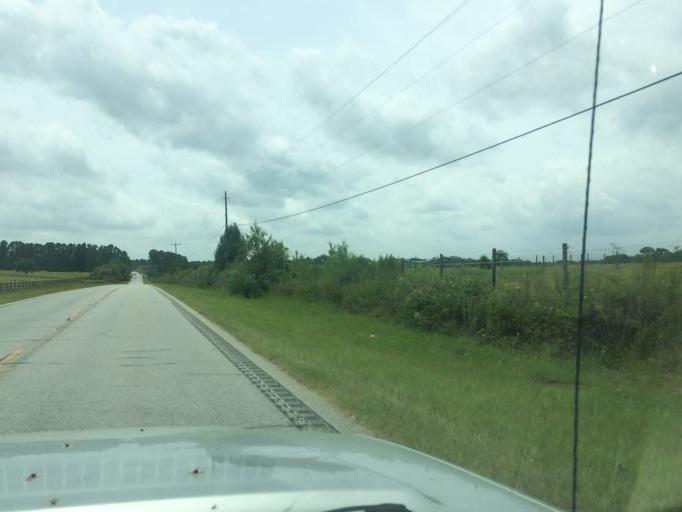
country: US
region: South Carolina
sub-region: Anderson County
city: Centerville
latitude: 34.4953
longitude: -82.7767
